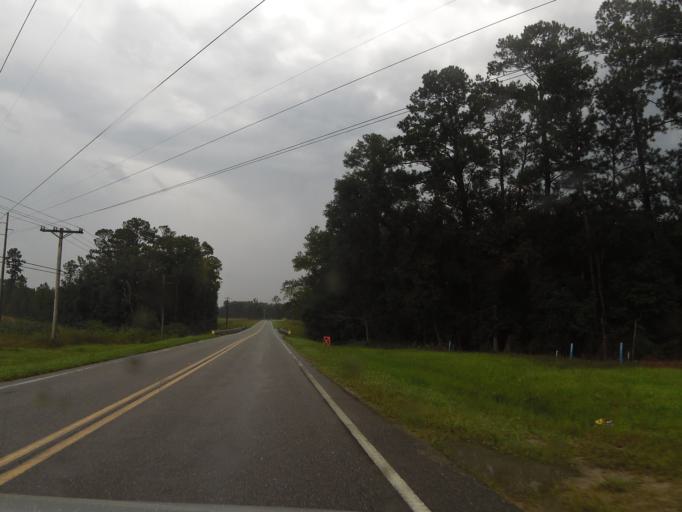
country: US
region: Florida
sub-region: Clay County
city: Middleburg
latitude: 30.0918
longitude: -81.8396
